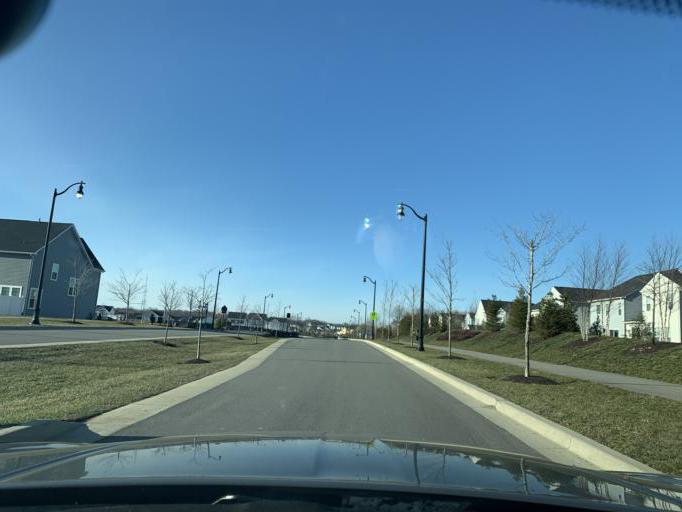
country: US
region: Maryland
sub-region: Anne Arundel County
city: Crofton
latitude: 39.0200
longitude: -76.7224
